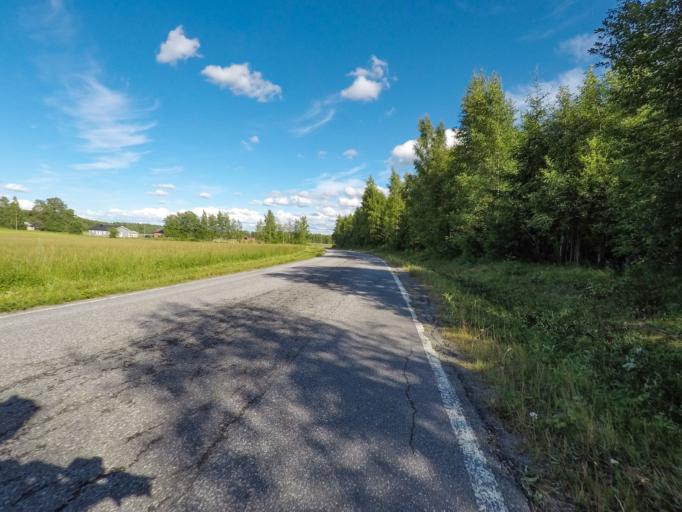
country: FI
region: South Karelia
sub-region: Imatra
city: Imatra
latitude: 61.1407
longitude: 28.6412
